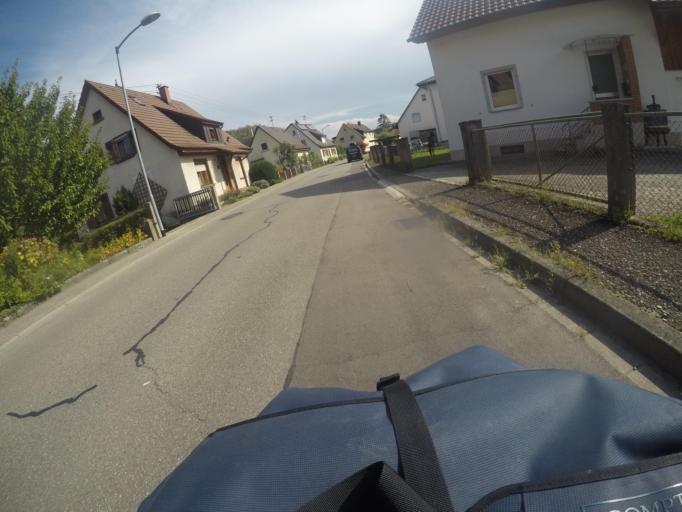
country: FR
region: Alsace
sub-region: Departement du Haut-Rhin
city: Rosenau
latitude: 47.6595
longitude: 7.5418
